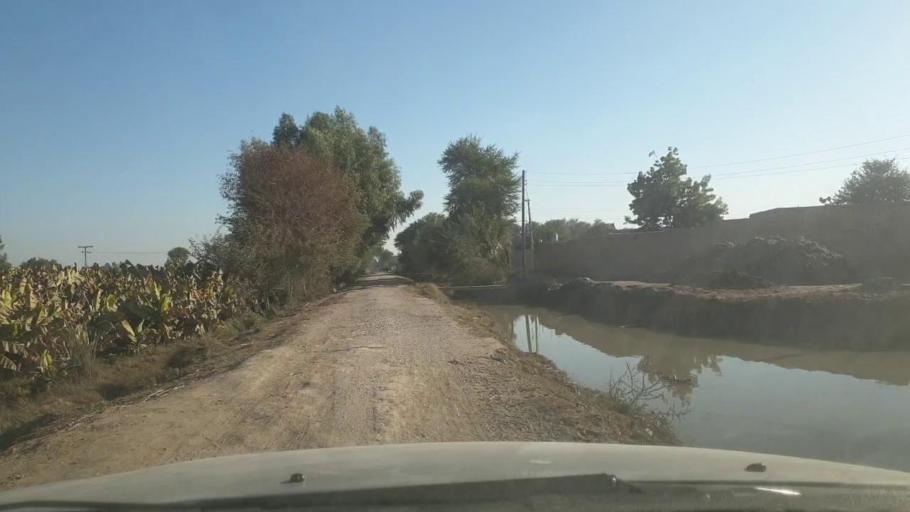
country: PK
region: Sindh
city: Adilpur
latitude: 27.9435
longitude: 69.2193
